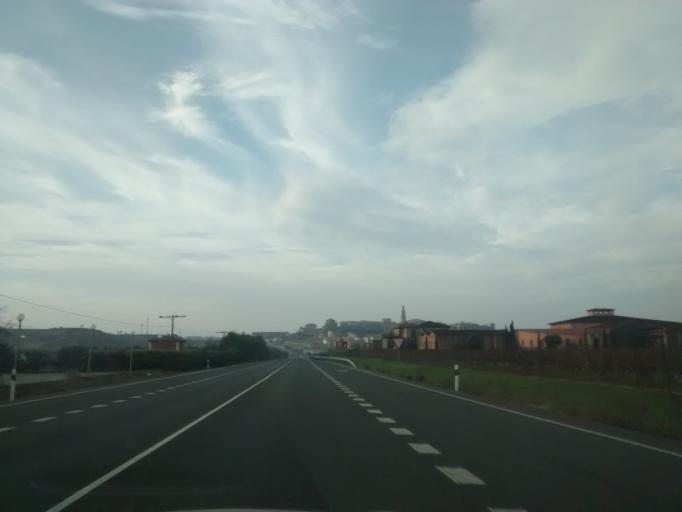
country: ES
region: La Rioja
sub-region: Provincia de La Rioja
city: Briones
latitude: 42.5365
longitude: -2.7736
